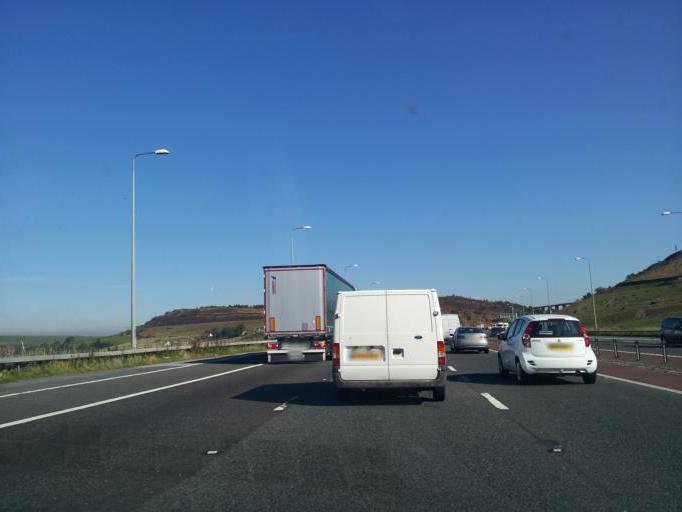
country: GB
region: England
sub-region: Calderdale
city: Ripponden
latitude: 53.6451
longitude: -1.9438
